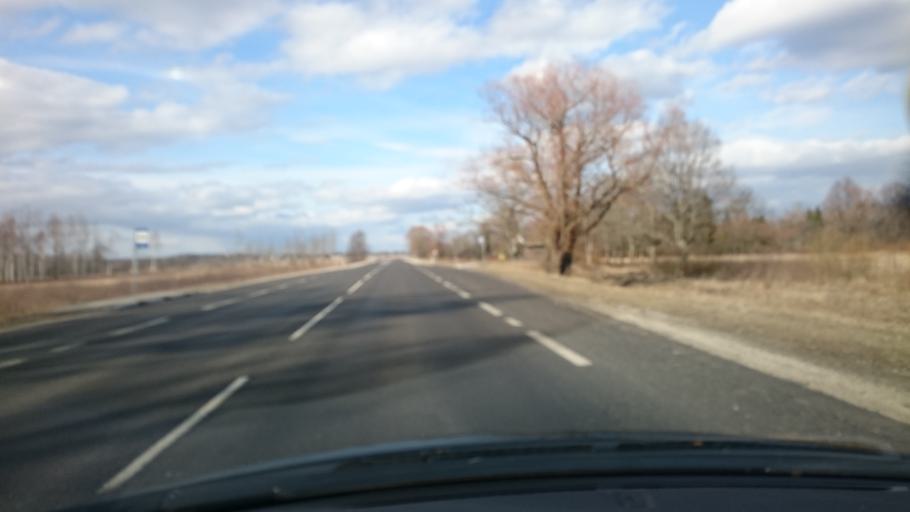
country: EE
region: Harju
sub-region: Nissi vald
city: Turba
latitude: 58.8570
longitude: 24.0719
